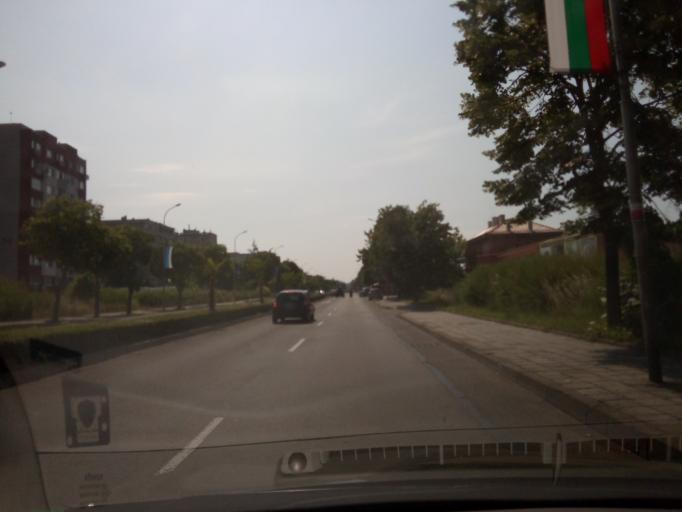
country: BG
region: Burgas
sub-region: Obshtina Pomorie
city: Pomorie
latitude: 42.5635
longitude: 27.6278
